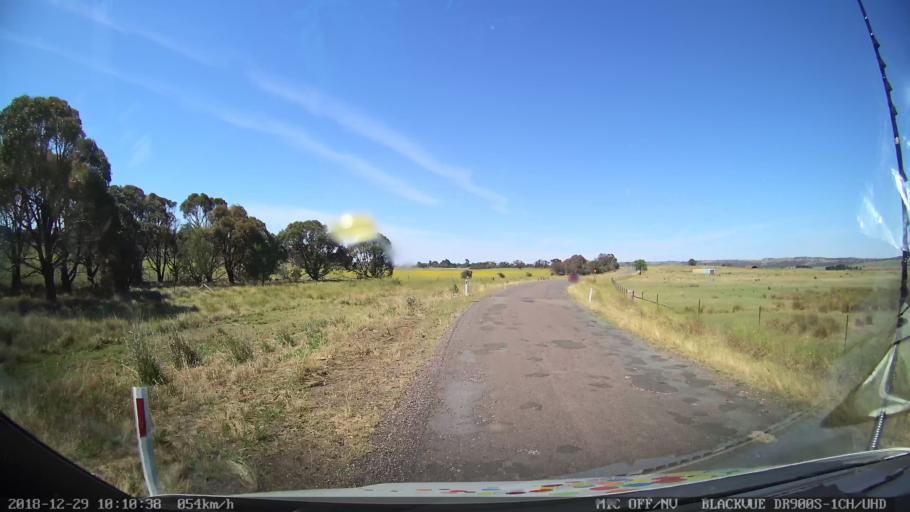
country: AU
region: New South Wales
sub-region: Yass Valley
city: Gundaroo
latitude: -34.8775
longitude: 149.4560
